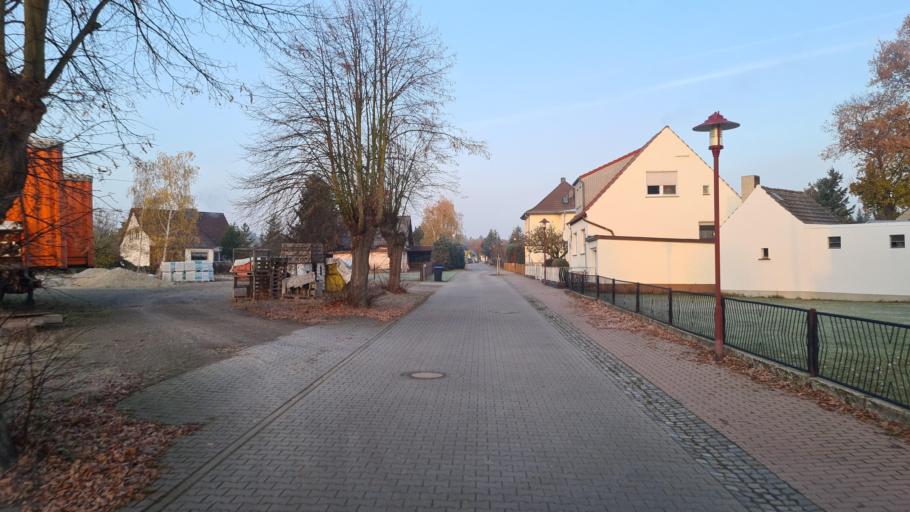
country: DE
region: Saxony-Anhalt
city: Jessen
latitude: 51.7971
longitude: 13.0128
